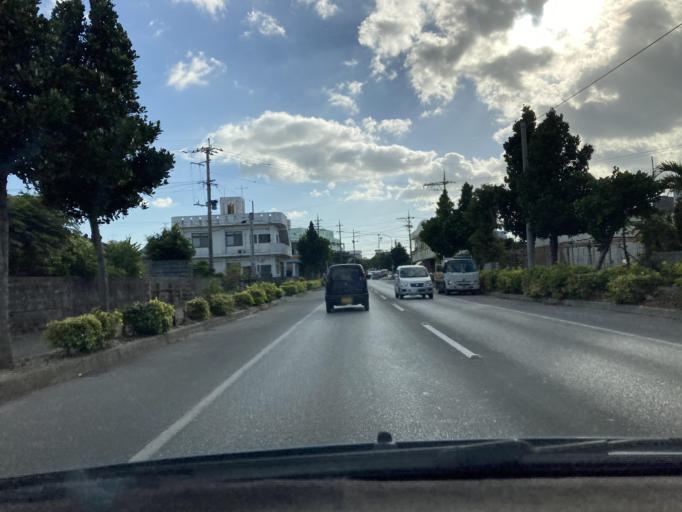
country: JP
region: Okinawa
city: Gushikawa
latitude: 26.3611
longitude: 127.8517
